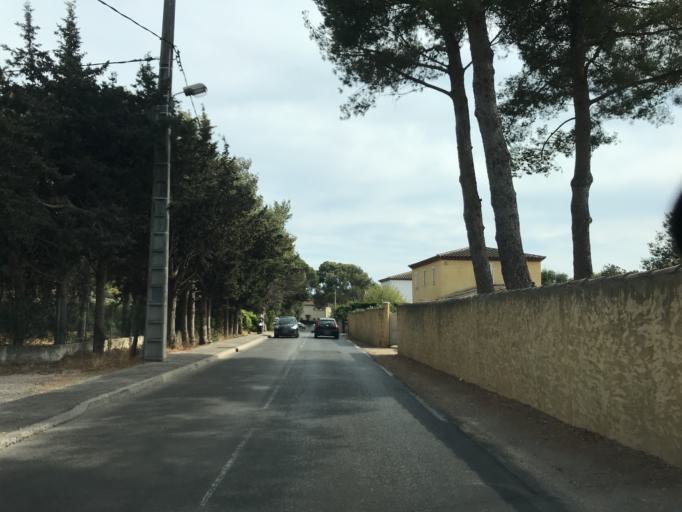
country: FR
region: Provence-Alpes-Cote d'Azur
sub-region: Departement du Var
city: La Seyne-sur-Mer
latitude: 43.0765
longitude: 5.8754
